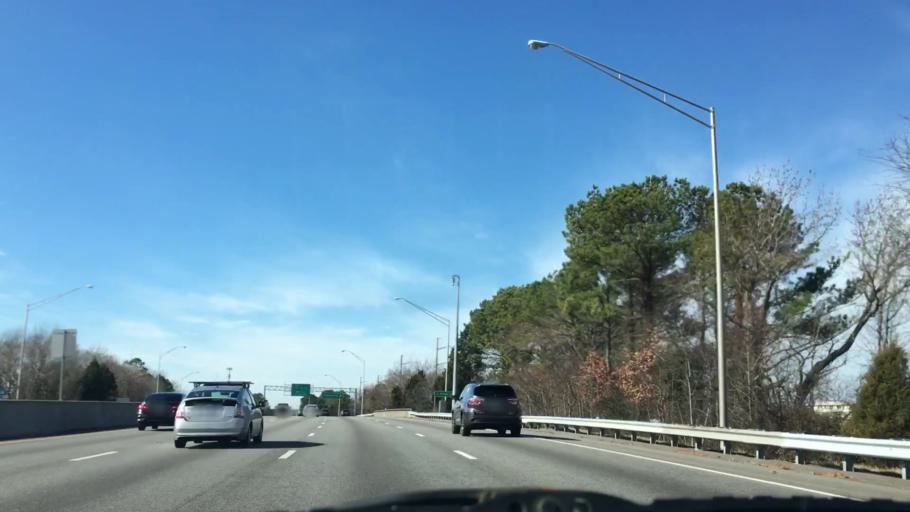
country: US
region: Virginia
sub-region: City of Virginia Beach
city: Virginia Beach
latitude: 36.8358
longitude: -76.0884
